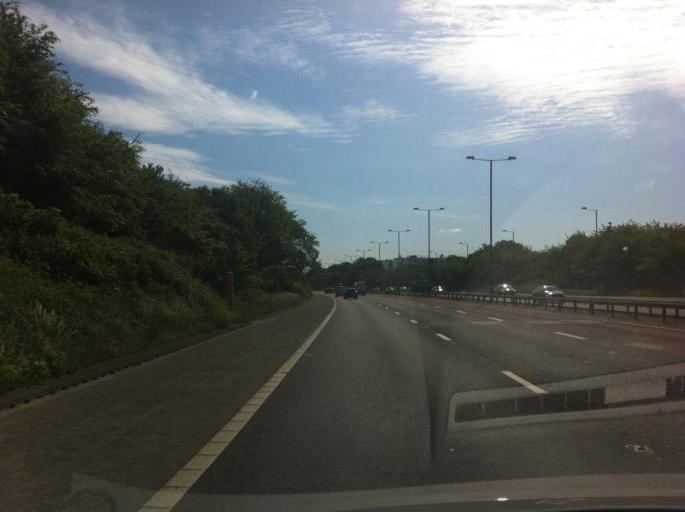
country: GB
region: England
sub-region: Greater London
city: Southall
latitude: 51.4881
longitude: -0.3906
